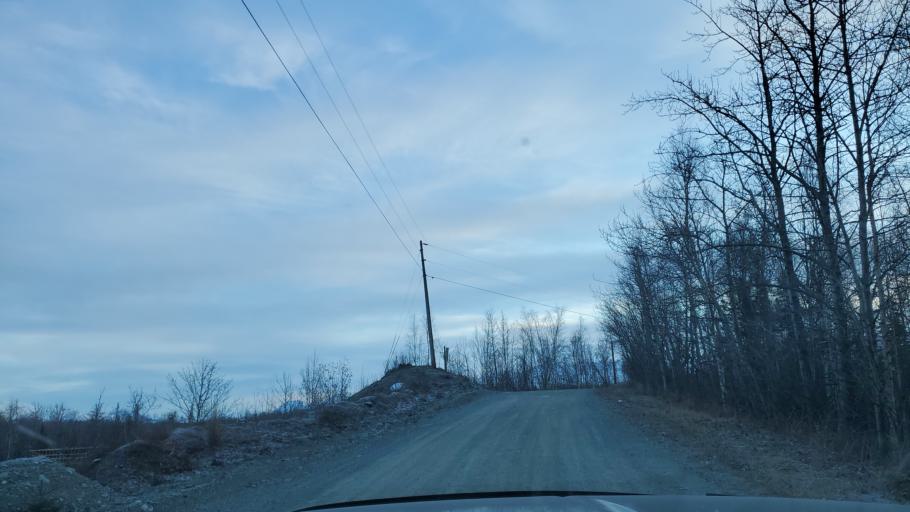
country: US
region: Alaska
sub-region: Matanuska-Susitna Borough
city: Lakes
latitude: 61.6023
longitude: -149.3133
